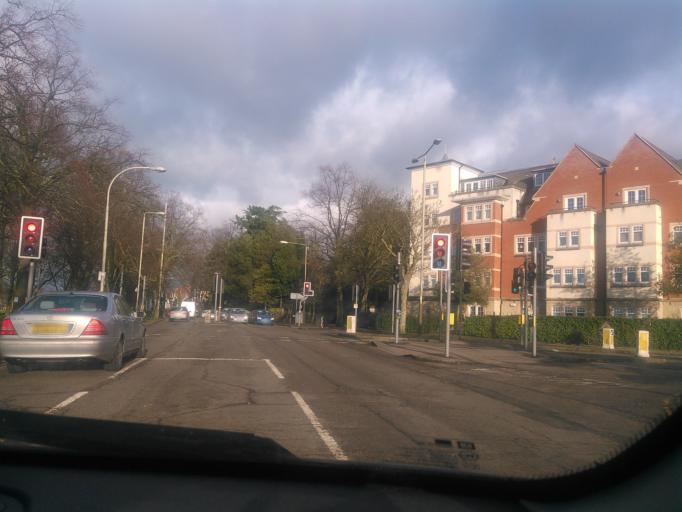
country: GB
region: England
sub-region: City of Leicester
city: Leicester
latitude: 52.6201
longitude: -1.1179
